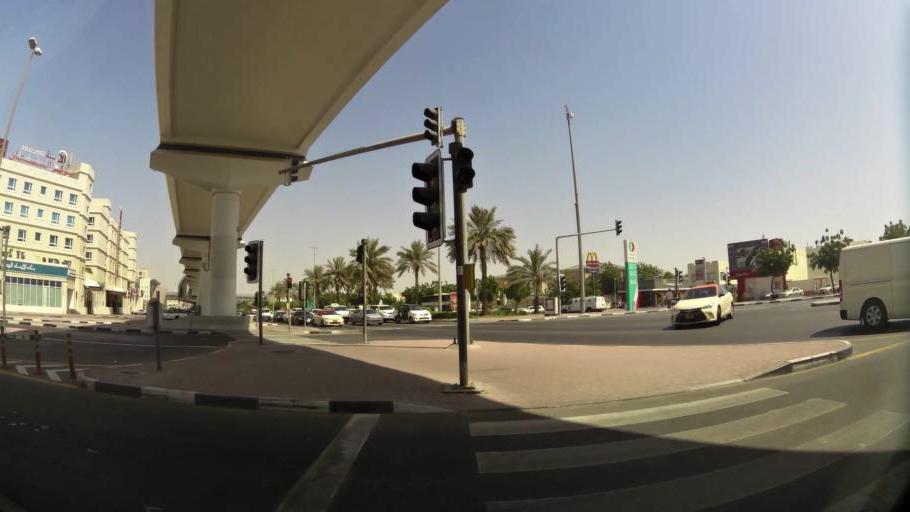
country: AE
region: Ash Shariqah
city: Sharjah
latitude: 25.2747
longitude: 55.3676
